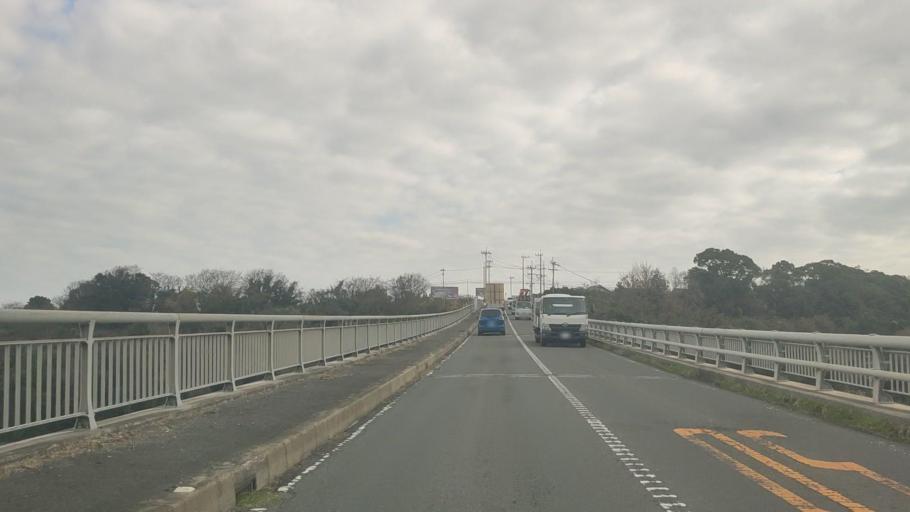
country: JP
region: Nagasaki
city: Shimabara
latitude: 32.8535
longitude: 130.2488
